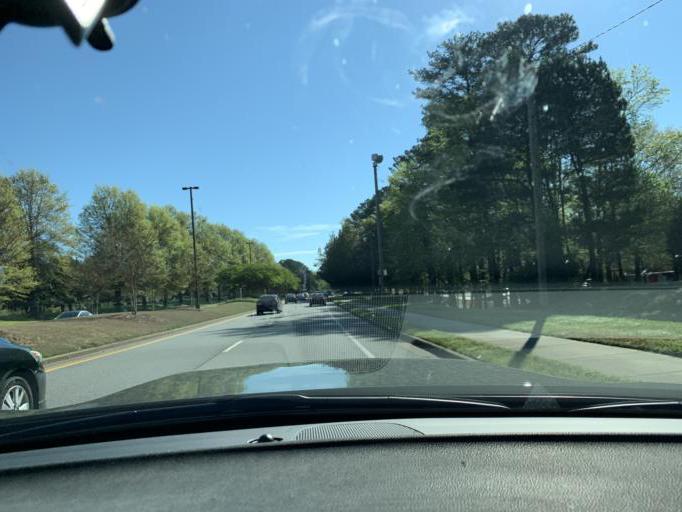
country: US
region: Georgia
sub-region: Fulton County
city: Alpharetta
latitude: 34.0891
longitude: -84.2548
